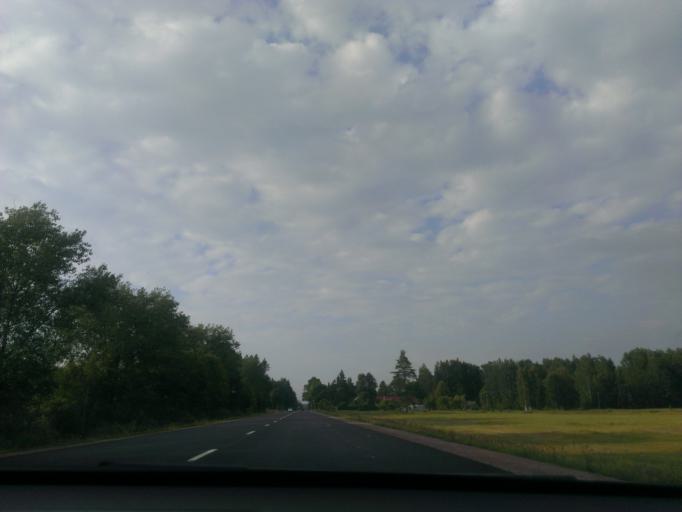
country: LV
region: Lecava
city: Iecava
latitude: 56.6907
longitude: 24.2410
